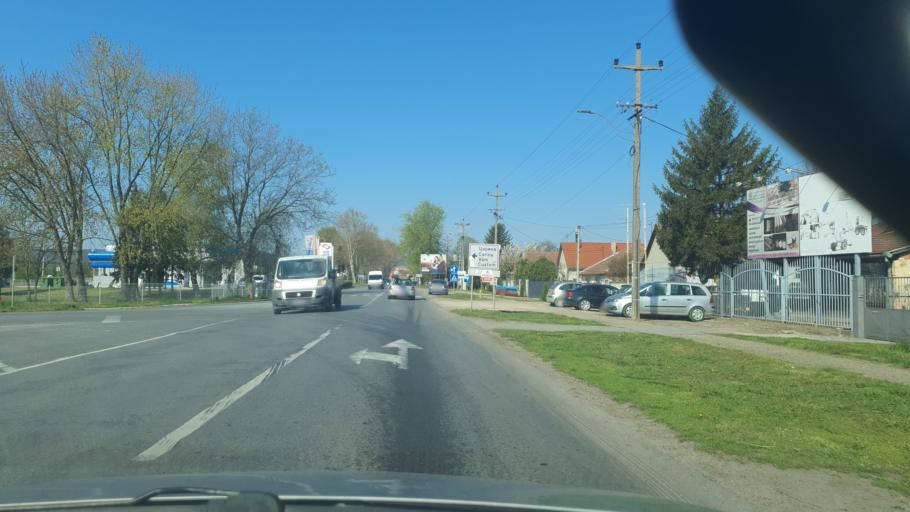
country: RS
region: Autonomna Pokrajina Vojvodina
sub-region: Zapadnobacki Okrug
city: Sombor
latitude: 45.7671
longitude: 19.1362
